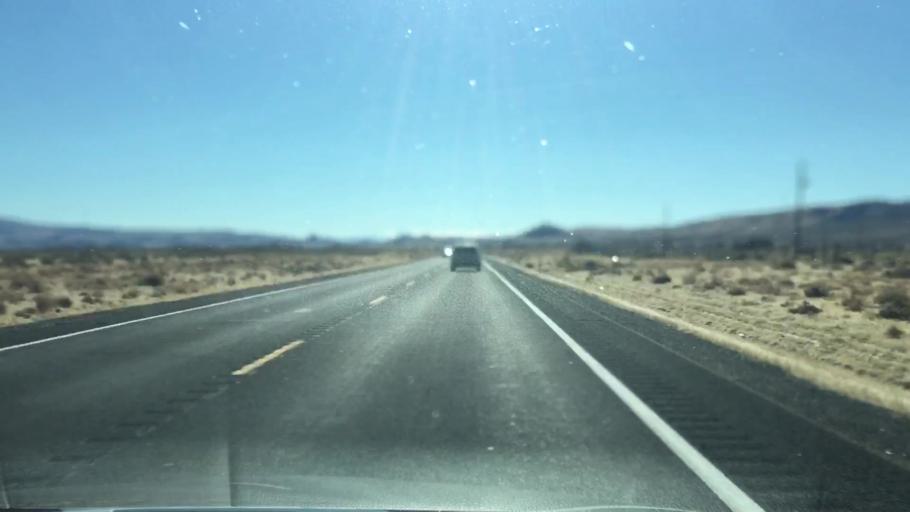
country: US
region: Nevada
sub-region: Lyon County
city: Silver Springs
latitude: 39.3852
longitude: -119.2315
